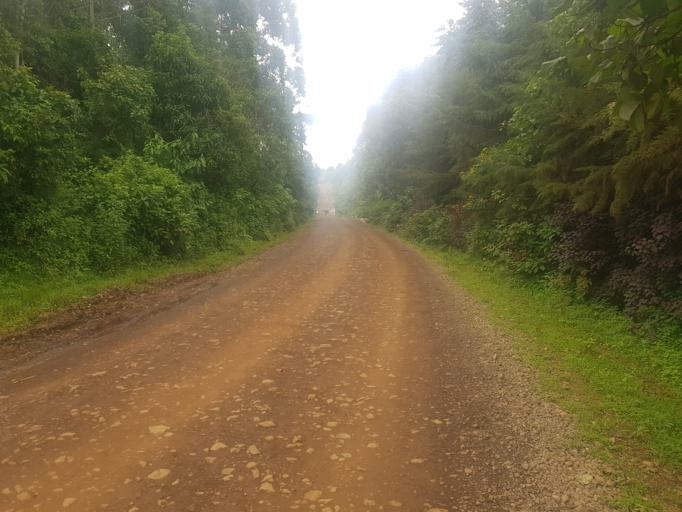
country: ET
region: Oromiya
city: Gore
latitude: 7.9103
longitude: 35.5122
